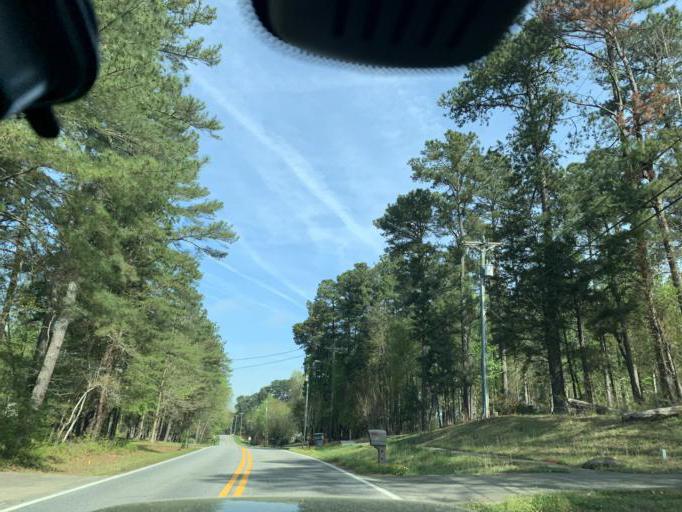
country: US
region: Georgia
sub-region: Forsyth County
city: Cumming
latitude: 34.2113
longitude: -84.0743
